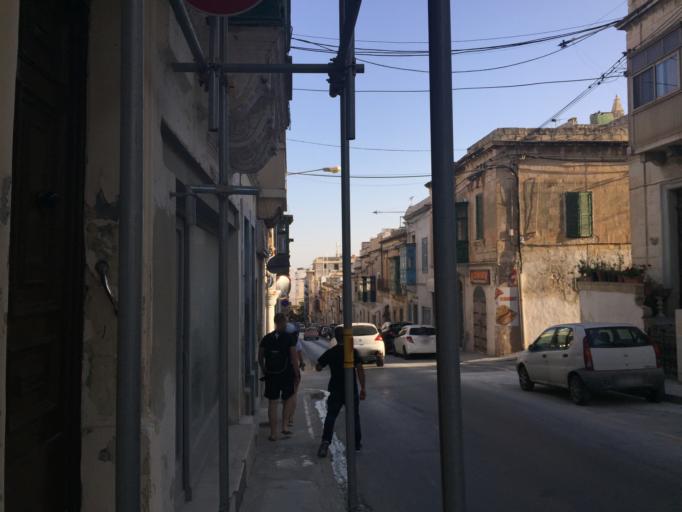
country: MT
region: Tas-Sliema
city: Sliema
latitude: 35.9113
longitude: 14.5016
